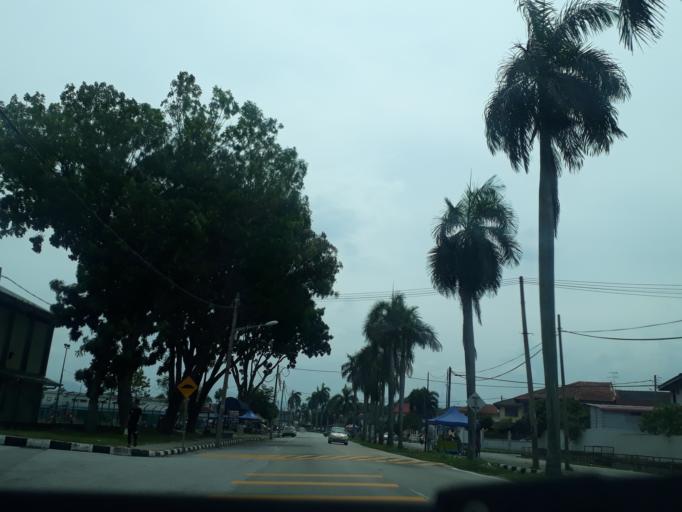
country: MY
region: Perak
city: Ipoh
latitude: 4.5938
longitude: 101.1300
